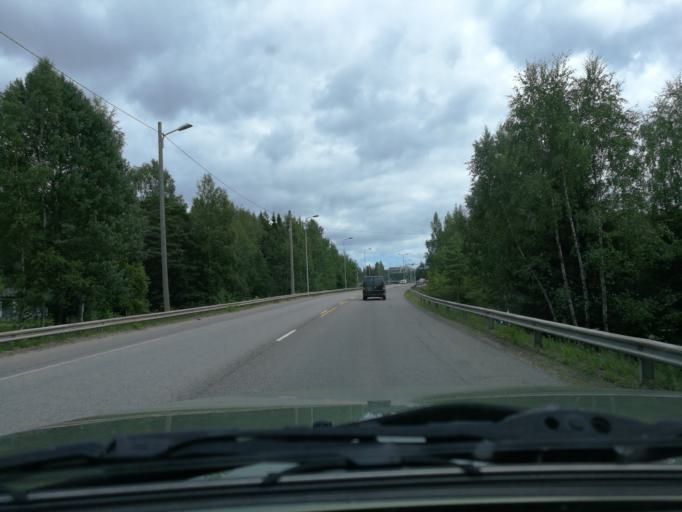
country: FI
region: Uusimaa
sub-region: Helsinki
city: Vantaa
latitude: 60.3115
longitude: 25.0922
